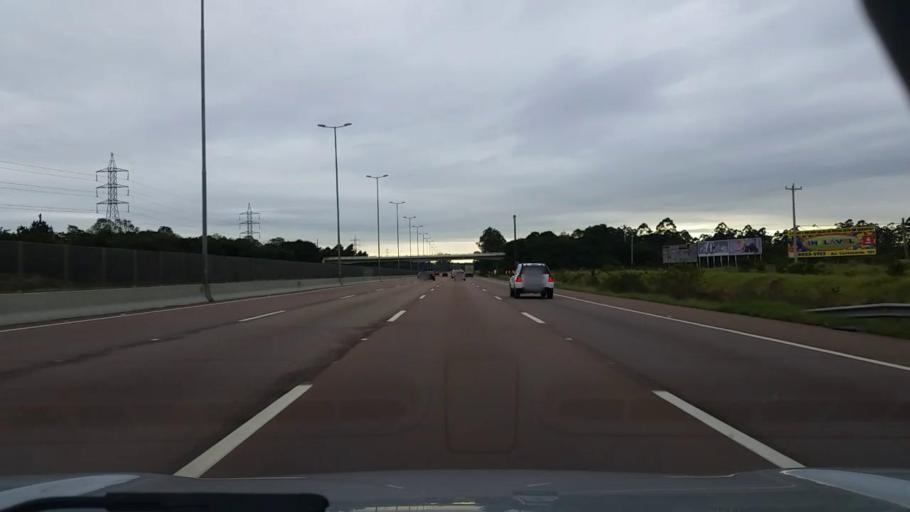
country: BR
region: Rio Grande do Sul
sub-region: Cachoeirinha
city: Cachoeirinha
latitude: -29.9539
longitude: -51.0612
